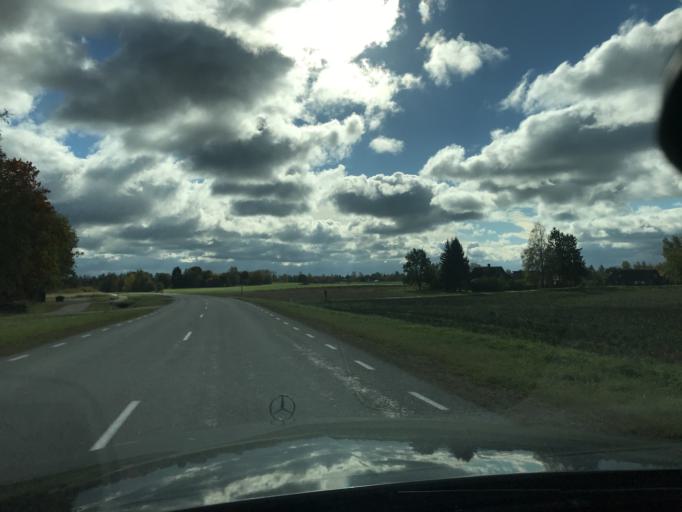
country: EE
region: Vorumaa
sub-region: Antsla vald
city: Vana-Antsla
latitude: 57.9327
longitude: 26.3169
